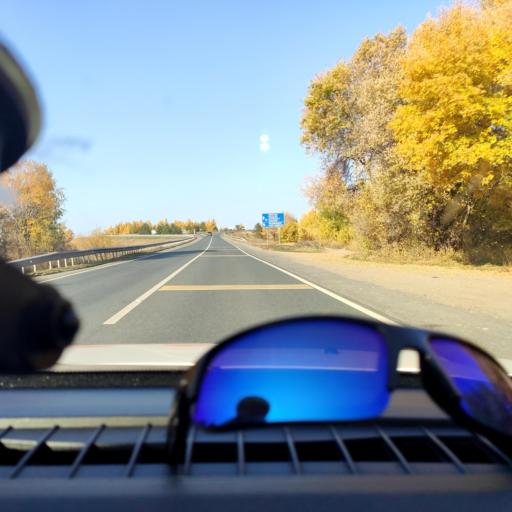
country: RU
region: Samara
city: Bereza
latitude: 53.4833
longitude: 50.1169
